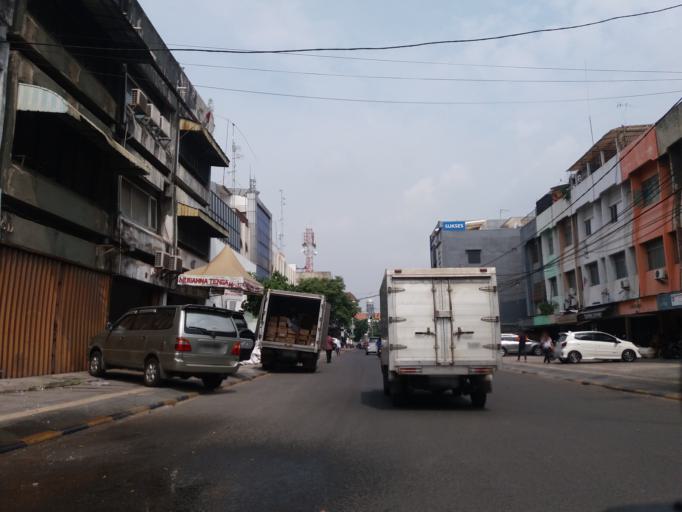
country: ID
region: Jakarta Raya
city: Jakarta
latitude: -6.1324
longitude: 106.8125
